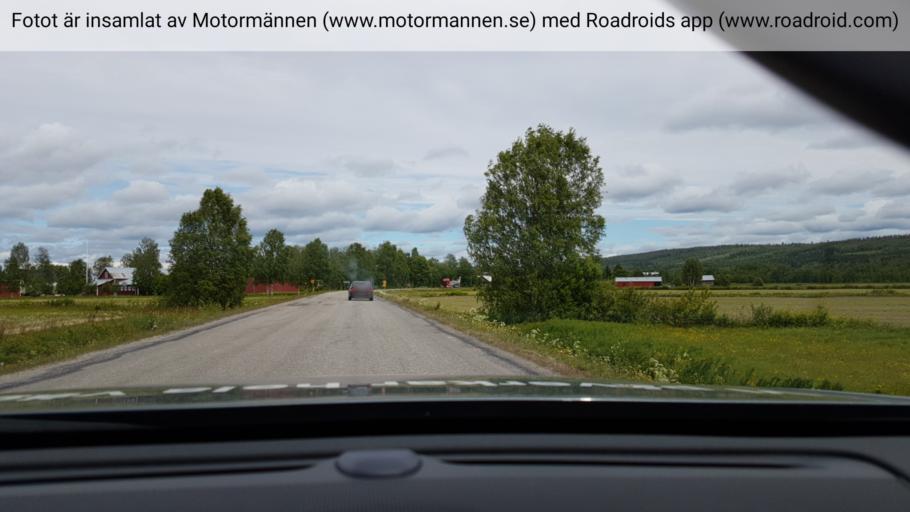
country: SE
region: Vaesterbotten
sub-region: Vannas Kommun
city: Vannasby
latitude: 63.9350
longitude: 19.8593
